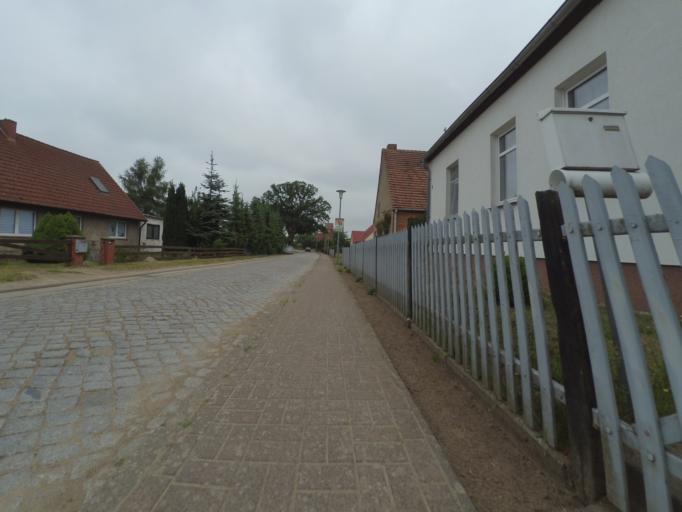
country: DE
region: Mecklenburg-Vorpommern
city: Goldberg
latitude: 53.4959
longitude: 12.1497
